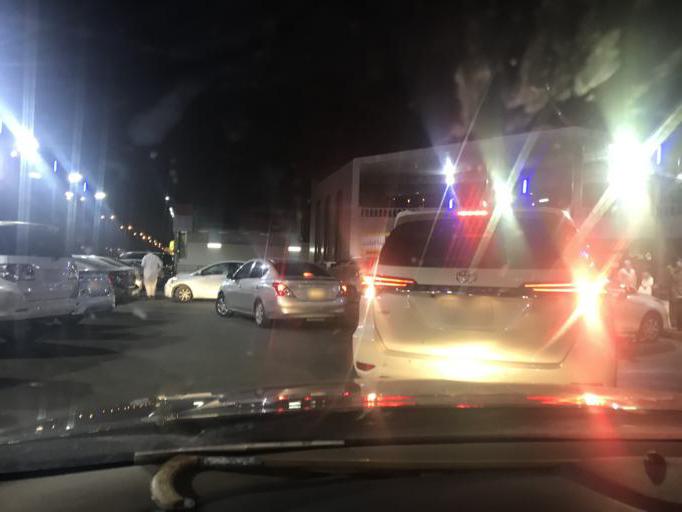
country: SA
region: Ar Riyad
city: Riyadh
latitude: 24.7474
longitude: 46.7756
